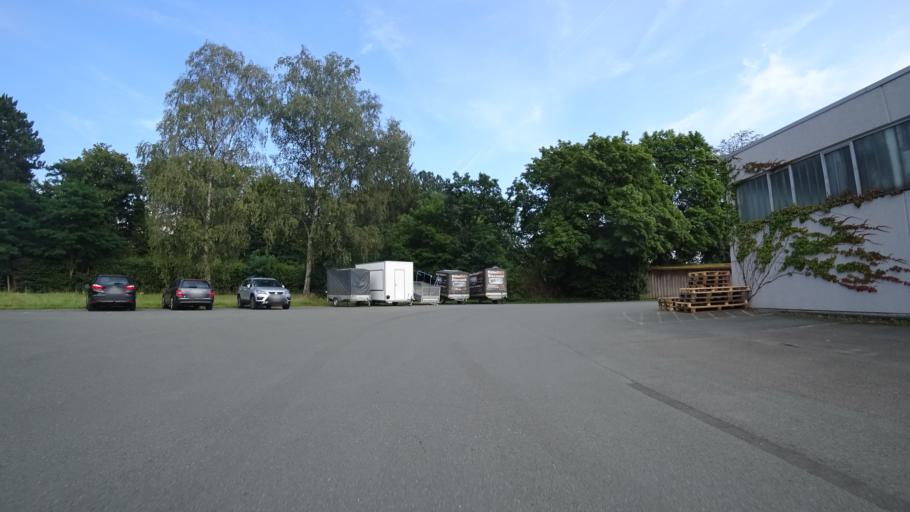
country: DE
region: North Rhine-Westphalia
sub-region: Regierungsbezirk Detmold
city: Guetersloh
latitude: 51.9388
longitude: 8.4235
